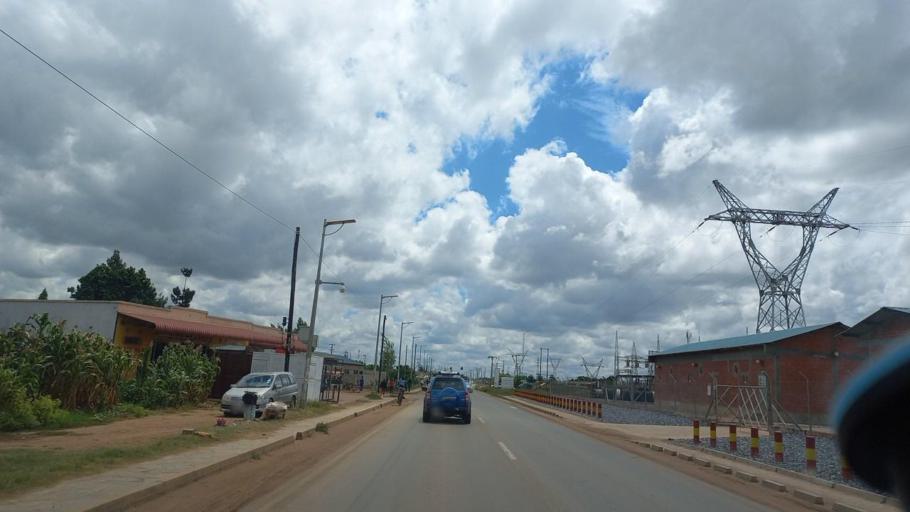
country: ZM
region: Lusaka
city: Lusaka
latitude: -15.4517
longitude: 28.3179
